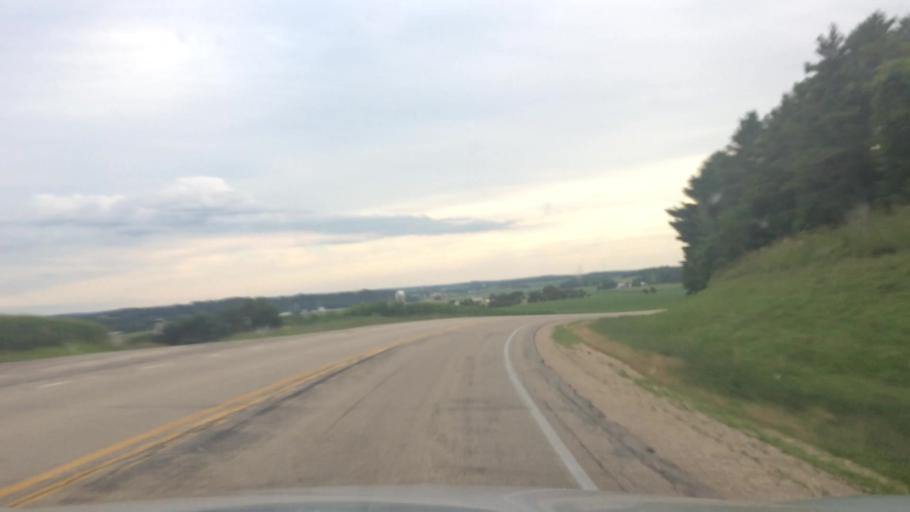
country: US
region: Wisconsin
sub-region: Columbia County
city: Lodi
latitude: 43.2385
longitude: -89.5211
